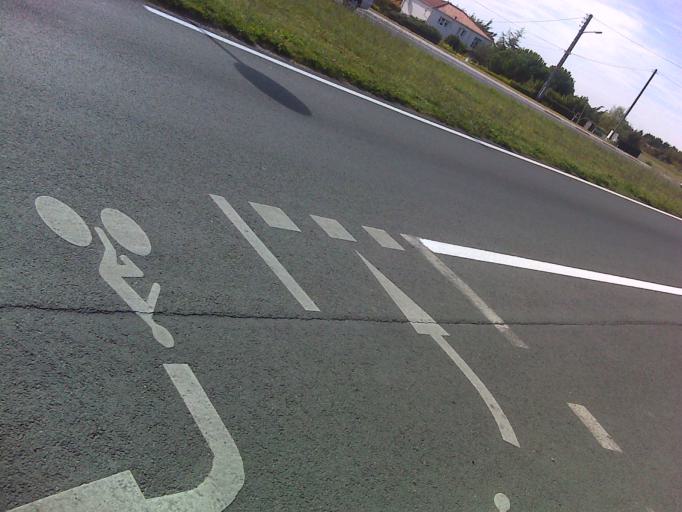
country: FR
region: Poitou-Charentes
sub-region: Departement de la Charente-Maritime
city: Marennes
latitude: 45.8309
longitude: -1.1208
